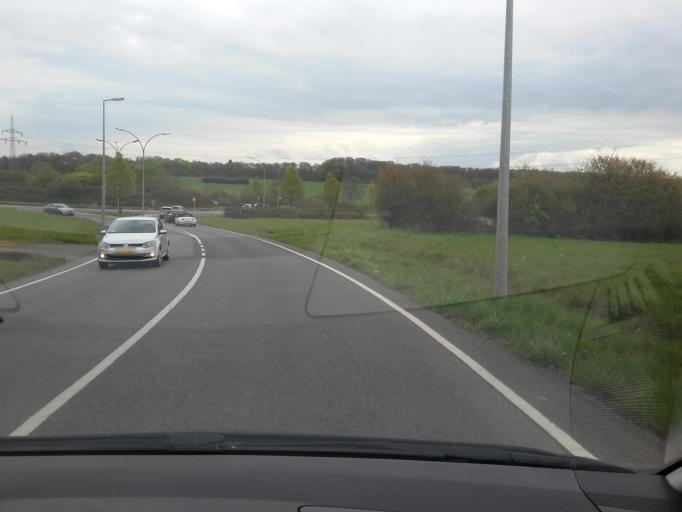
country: LU
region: Luxembourg
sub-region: Canton de Luxembourg
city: Bertrange
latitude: 49.5993
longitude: 6.0545
